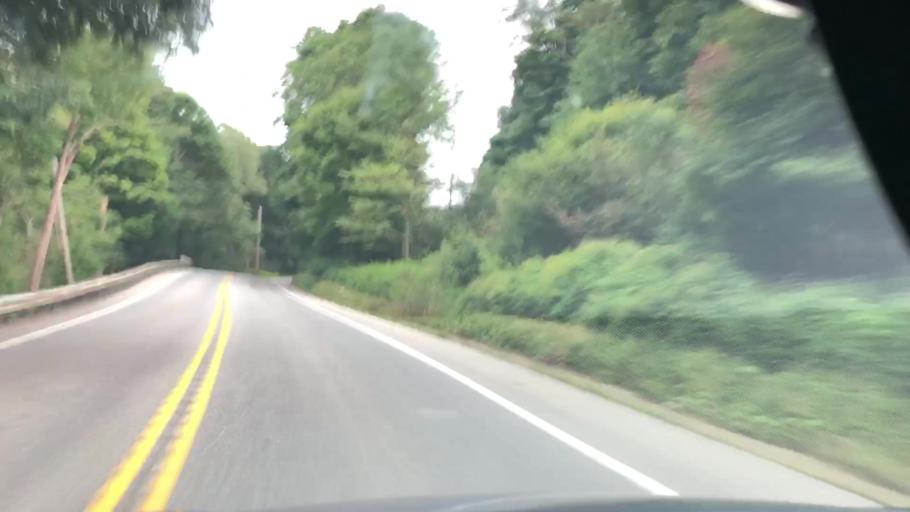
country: US
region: Pennsylvania
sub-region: Venango County
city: Hasson Heights
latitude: 41.5135
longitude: -79.7040
